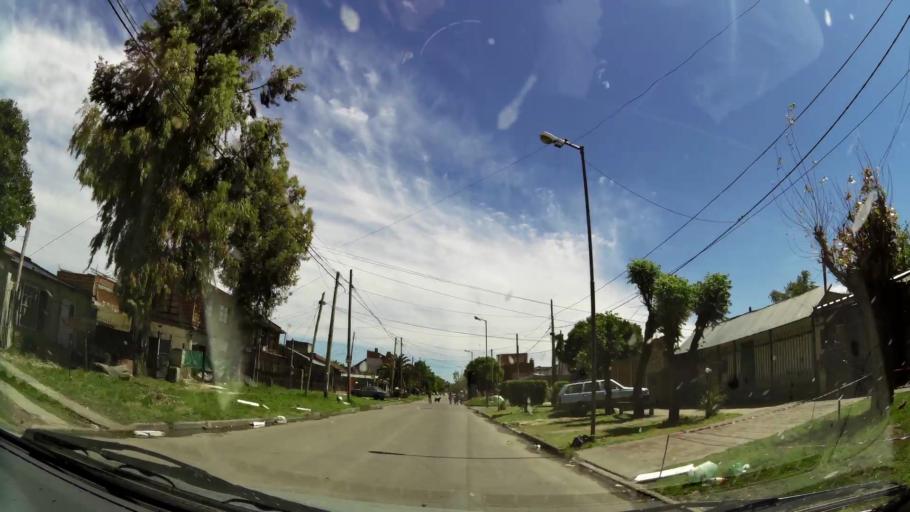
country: AR
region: Buenos Aires
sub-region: Partido de Quilmes
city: Quilmes
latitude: -34.7351
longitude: -58.3033
